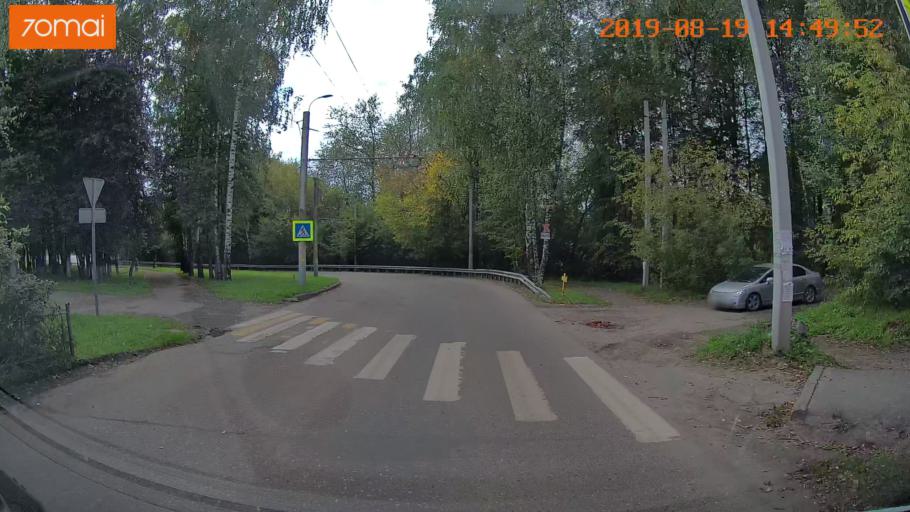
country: RU
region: Ivanovo
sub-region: Gorod Ivanovo
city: Ivanovo
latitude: 56.9945
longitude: 41.0199
